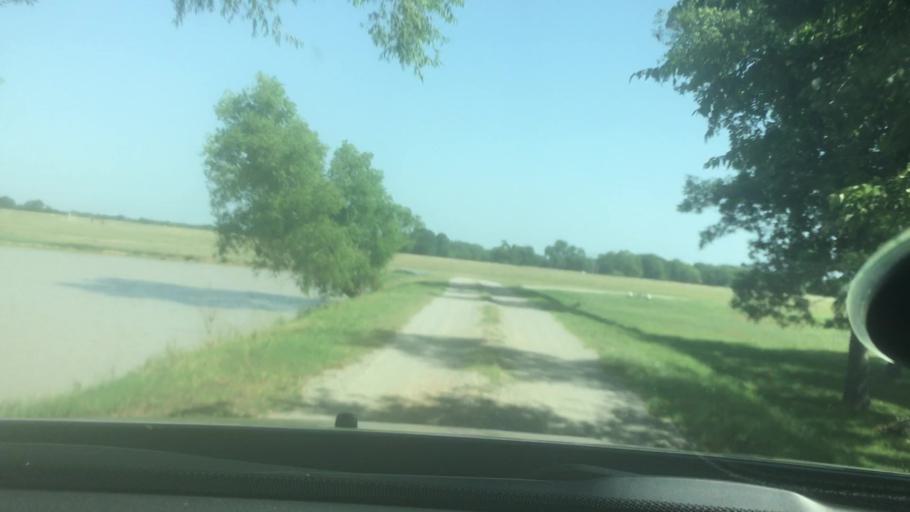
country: US
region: Oklahoma
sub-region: Bryan County
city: Durant
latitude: 34.1300
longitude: -96.3998
